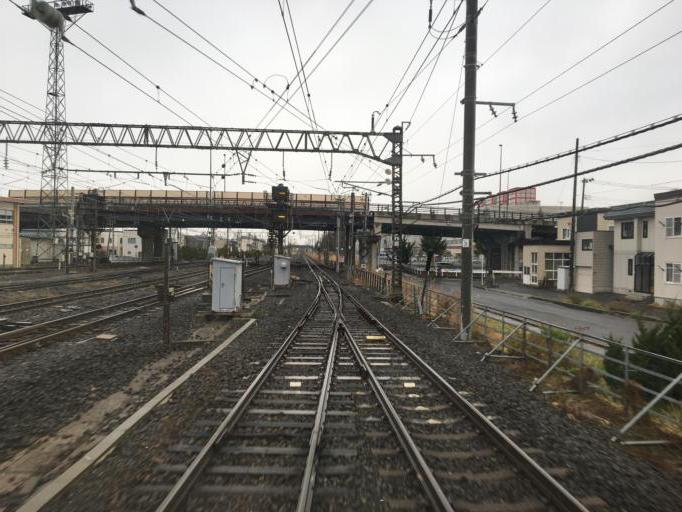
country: JP
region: Aomori
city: Aomori Shi
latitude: 40.8133
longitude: 140.7887
